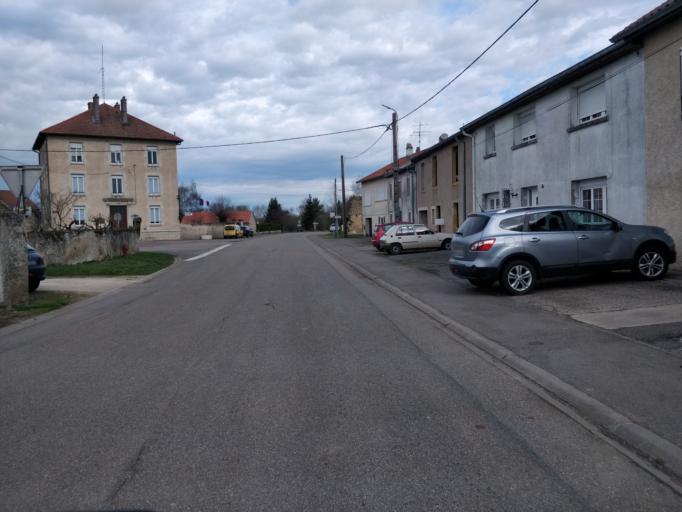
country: FR
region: Lorraine
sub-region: Departement de Meurthe-et-Moselle
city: Jarny
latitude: 49.1001
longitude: 5.8902
